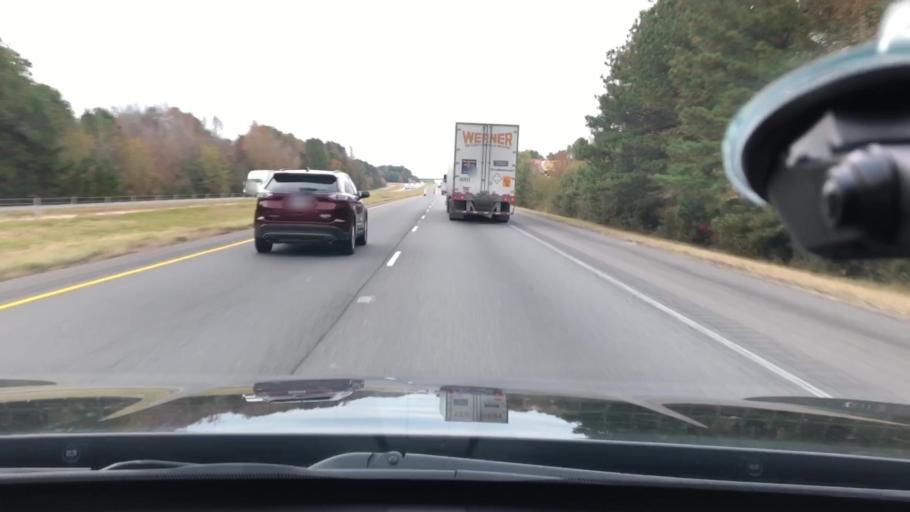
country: US
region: Arkansas
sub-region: Clark County
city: Arkadelphia
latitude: 34.0637
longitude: -93.1260
